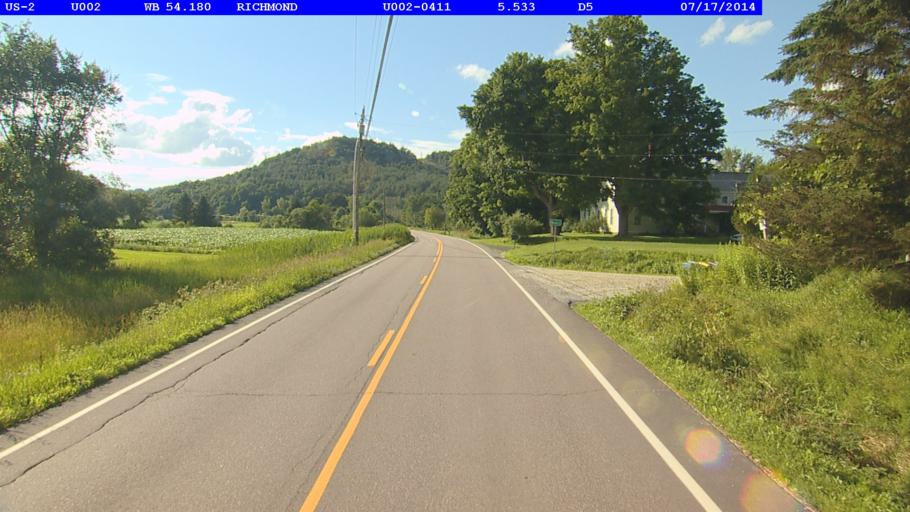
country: US
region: Vermont
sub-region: Chittenden County
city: Jericho
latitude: 44.3911
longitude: -72.9445
